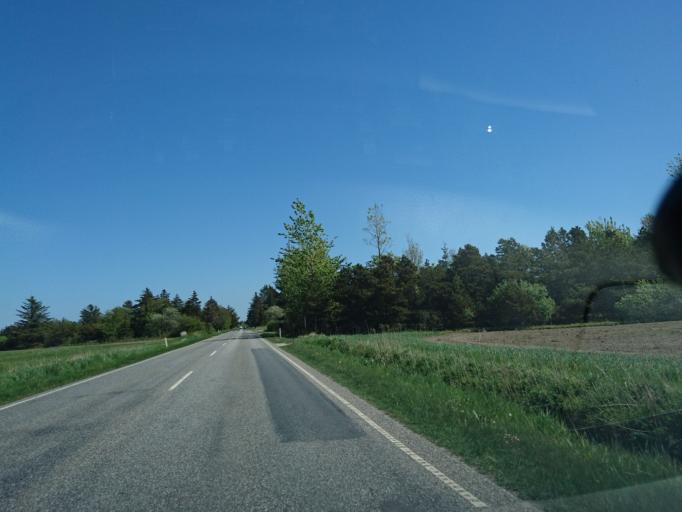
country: DK
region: North Denmark
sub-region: Hjorring Kommune
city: Sindal
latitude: 57.5758
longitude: 10.1554
